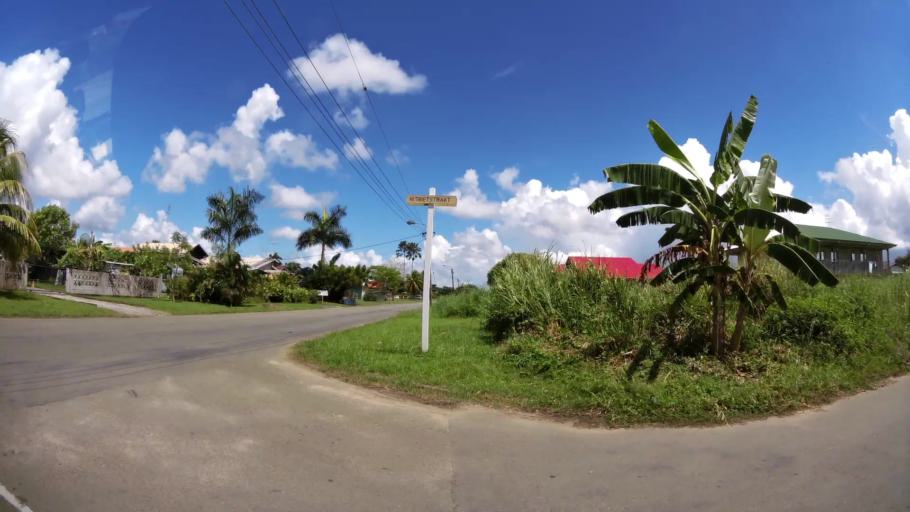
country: SR
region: Paramaribo
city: Paramaribo
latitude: 5.8641
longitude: -55.1437
